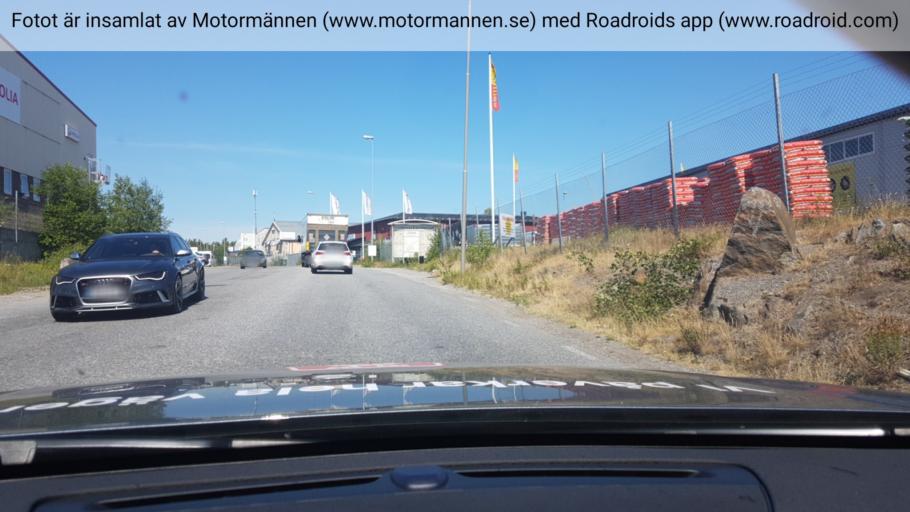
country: SE
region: Stockholm
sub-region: Haninge Kommun
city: Handen
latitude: 59.1967
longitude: 18.1197
